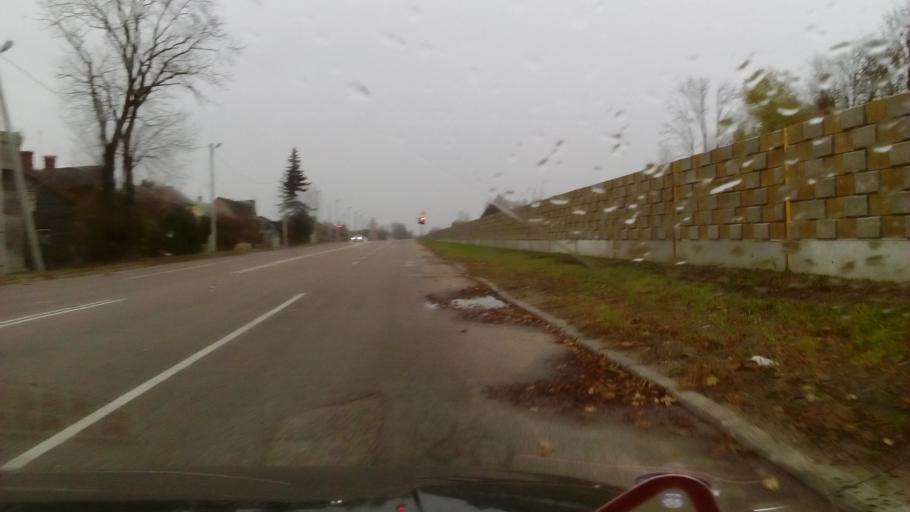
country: LT
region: Marijampoles apskritis
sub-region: Marijampole Municipality
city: Marijampole
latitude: 54.5459
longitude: 23.3567
